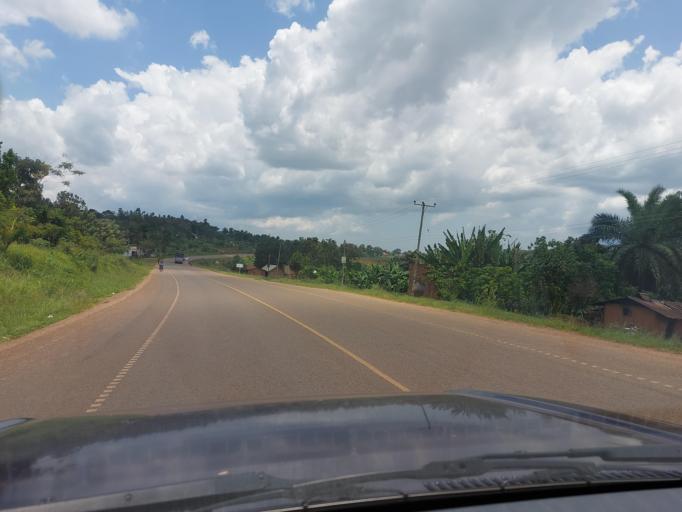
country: UG
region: Central Region
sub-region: Mukono District
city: Mukono
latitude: 0.3114
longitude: 32.7740
